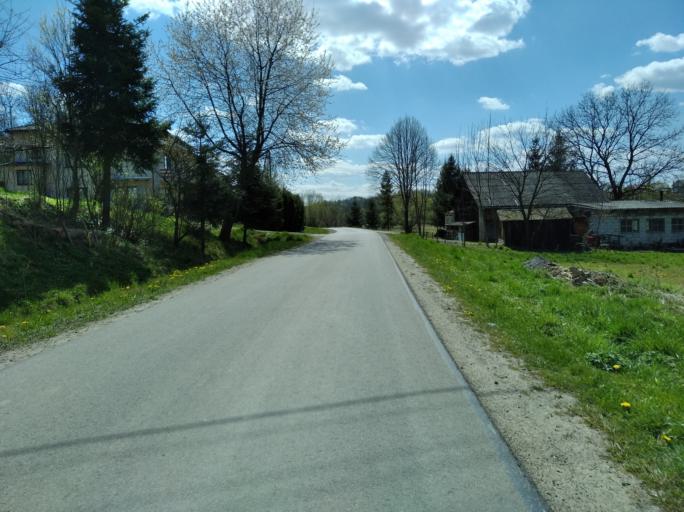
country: PL
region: Subcarpathian Voivodeship
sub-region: Powiat brzozowski
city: Domaradz
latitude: 49.7865
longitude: 21.9549
